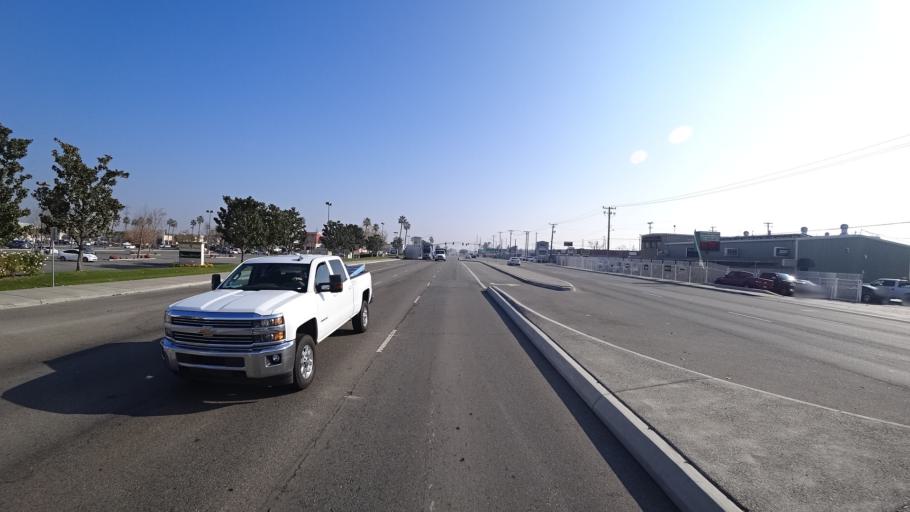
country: US
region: California
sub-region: Kern County
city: Greenacres
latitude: 35.3835
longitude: -119.1064
